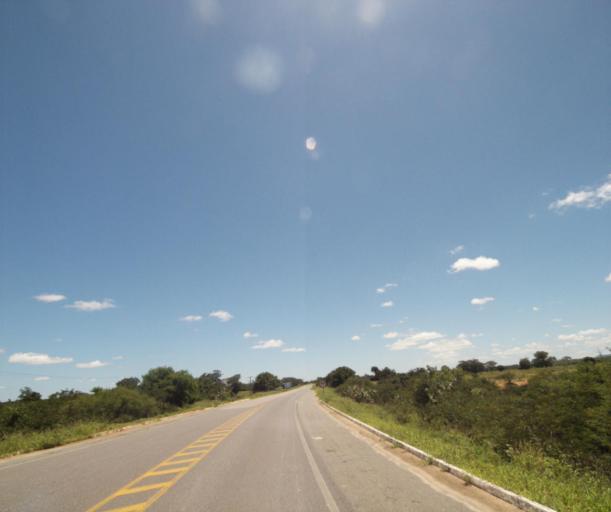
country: BR
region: Bahia
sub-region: Carinhanha
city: Carinhanha
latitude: -14.3270
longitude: -43.7612
